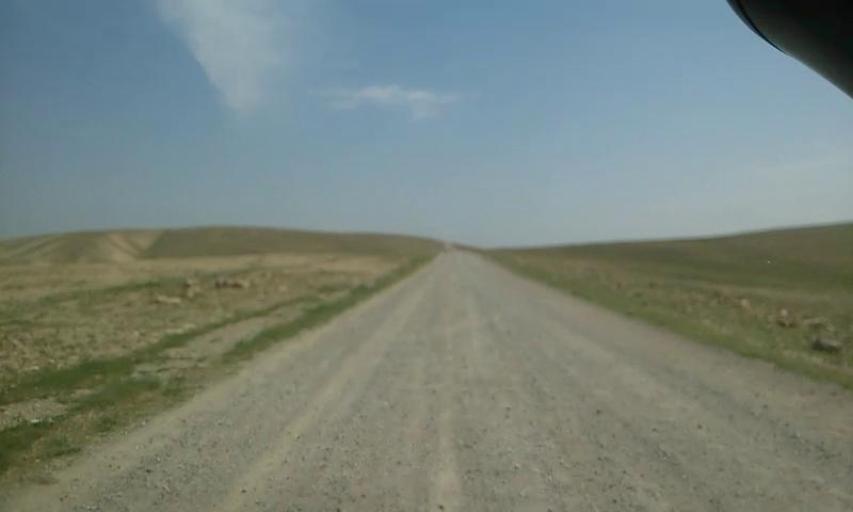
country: PS
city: `Arab ar Rashaydah
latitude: 31.5264
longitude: 35.2951
